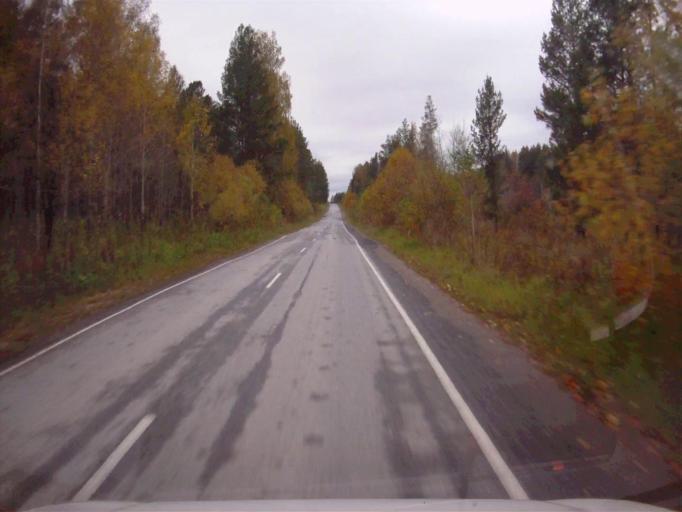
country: RU
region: Chelyabinsk
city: Nyazepetrovsk
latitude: 56.0529
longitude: 59.4820
